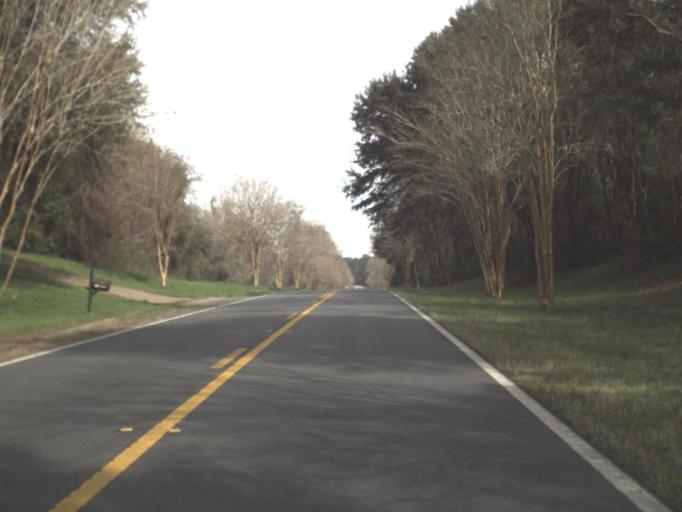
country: US
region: Florida
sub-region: Jefferson County
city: Monticello
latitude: 30.5288
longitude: -83.9839
